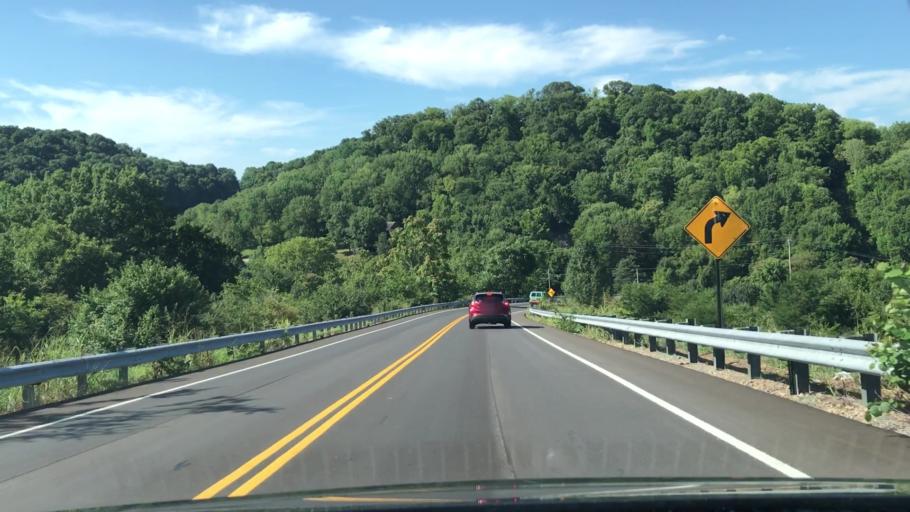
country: US
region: Tennessee
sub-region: Williamson County
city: Franklin
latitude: 35.9738
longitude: -86.8594
